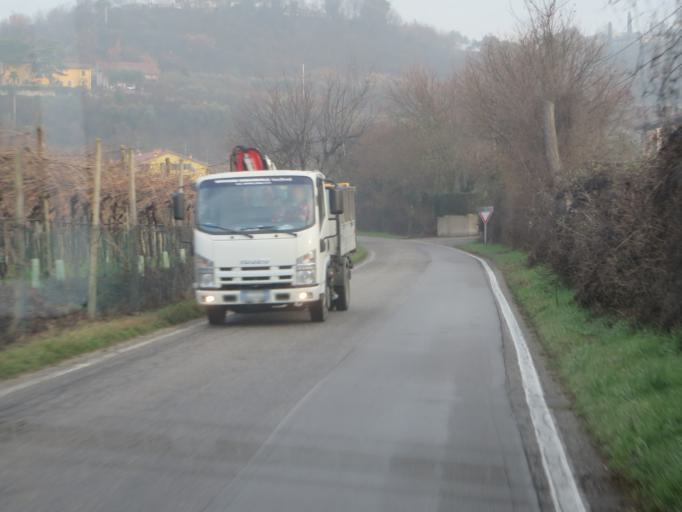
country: IT
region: Veneto
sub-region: Provincia di Verona
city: Pastrengo
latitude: 45.4811
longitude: 10.8072
